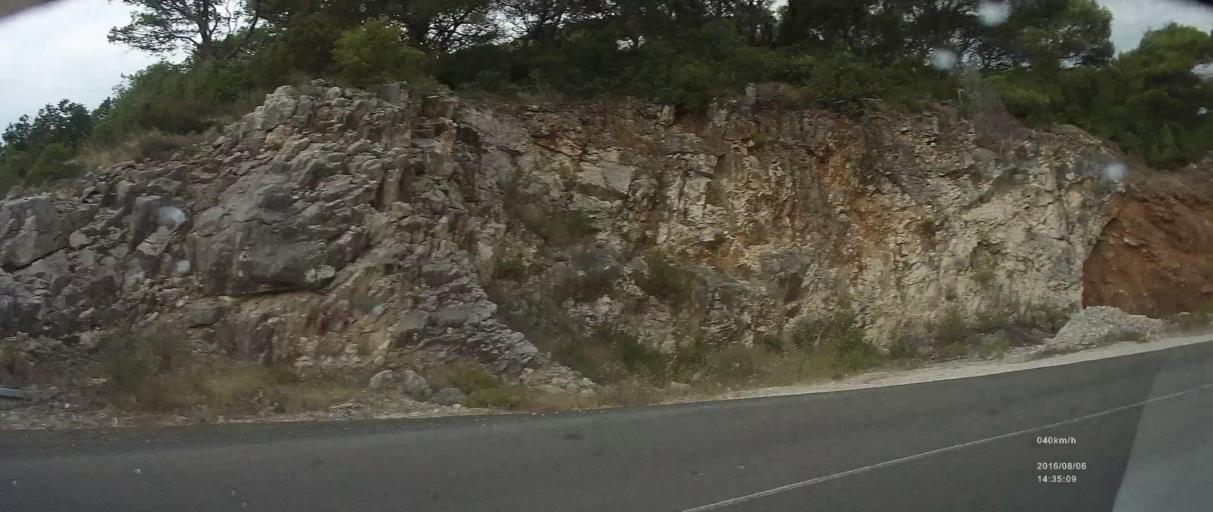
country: HR
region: Dubrovacko-Neretvanska
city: Ston
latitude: 42.7102
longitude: 17.6941
